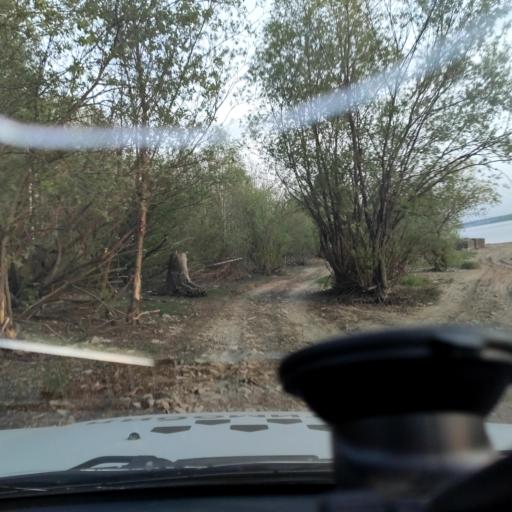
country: RU
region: Perm
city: Perm
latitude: 58.1102
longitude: 56.3387
